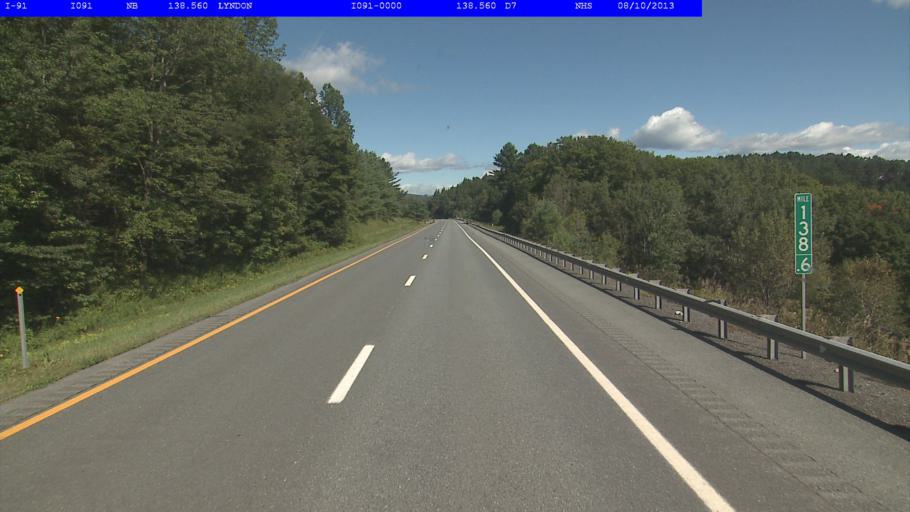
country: US
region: Vermont
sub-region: Caledonia County
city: Lyndonville
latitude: 44.5358
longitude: -72.0180
